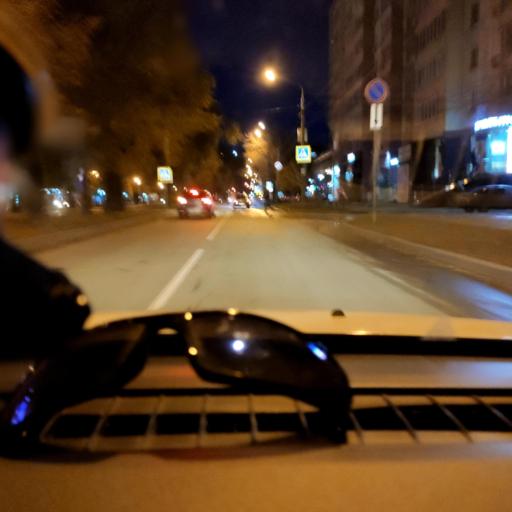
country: RU
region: Samara
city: Samara
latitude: 53.1980
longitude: 50.1787
